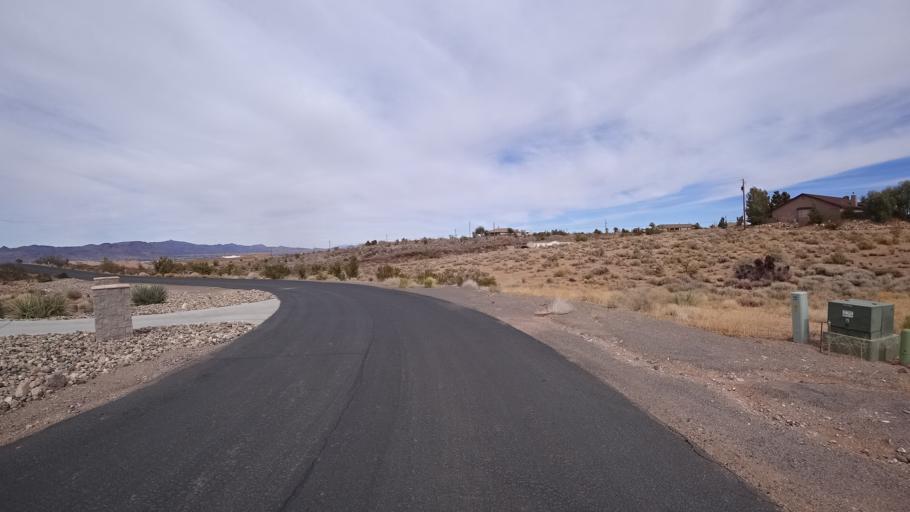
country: US
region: Arizona
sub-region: Mohave County
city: Kingman
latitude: 35.1766
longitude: -113.9946
